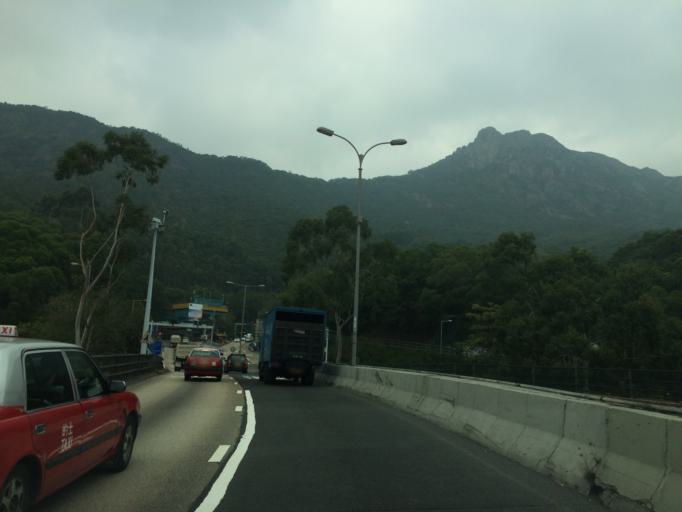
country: HK
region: Wong Tai Sin
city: Wong Tai Sin
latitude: 22.3439
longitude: 114.1817
